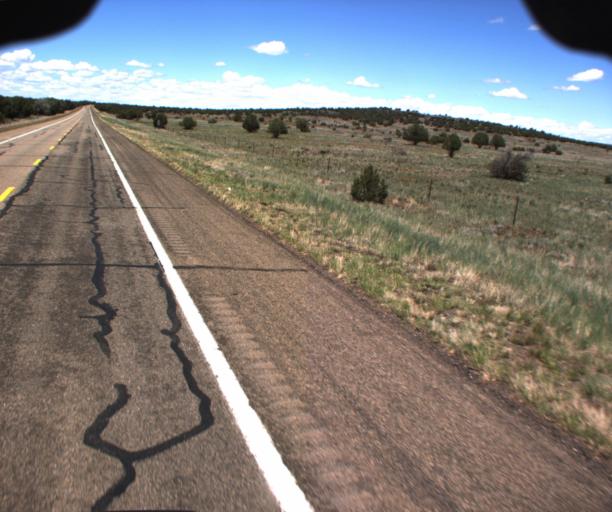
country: US
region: Arizona
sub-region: Yavapai County
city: Paulden
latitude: 35.1533
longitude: -112.4515
